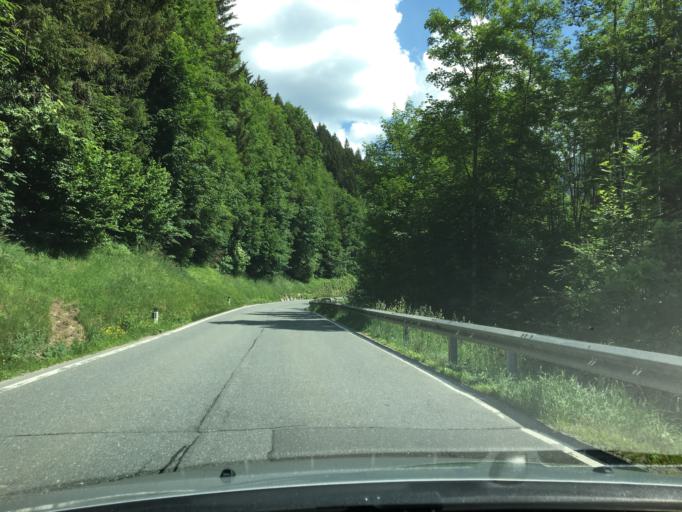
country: AT
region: Salzburg
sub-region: Politischer Bezirk Sankt Johann im Pongau
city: Sankt Johann im Pongau
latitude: 47.3429
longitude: 13.2100
